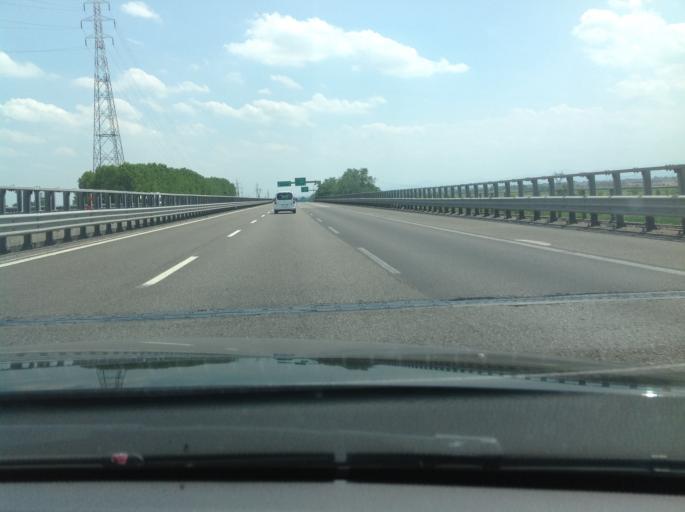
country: IT
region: Emilia-Romagna
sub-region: Provincia di Piacenza
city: Piacenza
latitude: 45.0639
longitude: 9.7360
